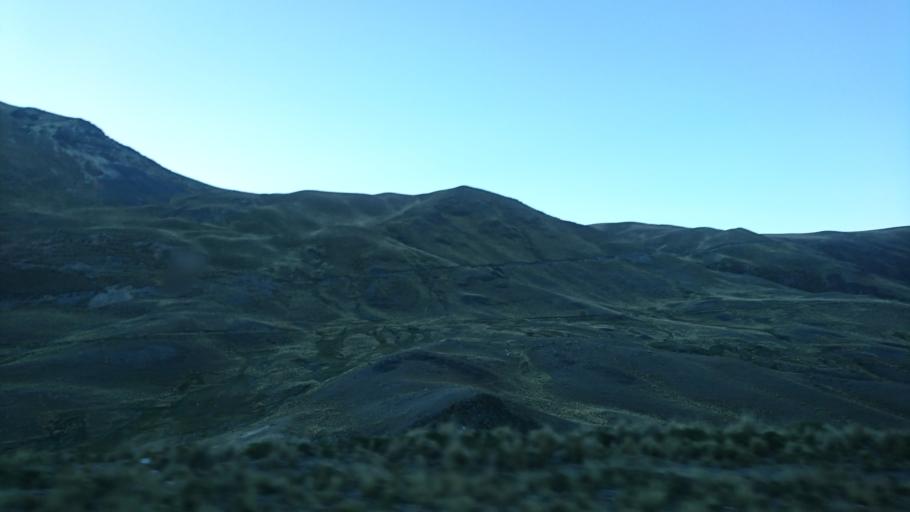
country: BO
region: La Paz
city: La Paz
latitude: -16.4121
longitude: -68.0515
